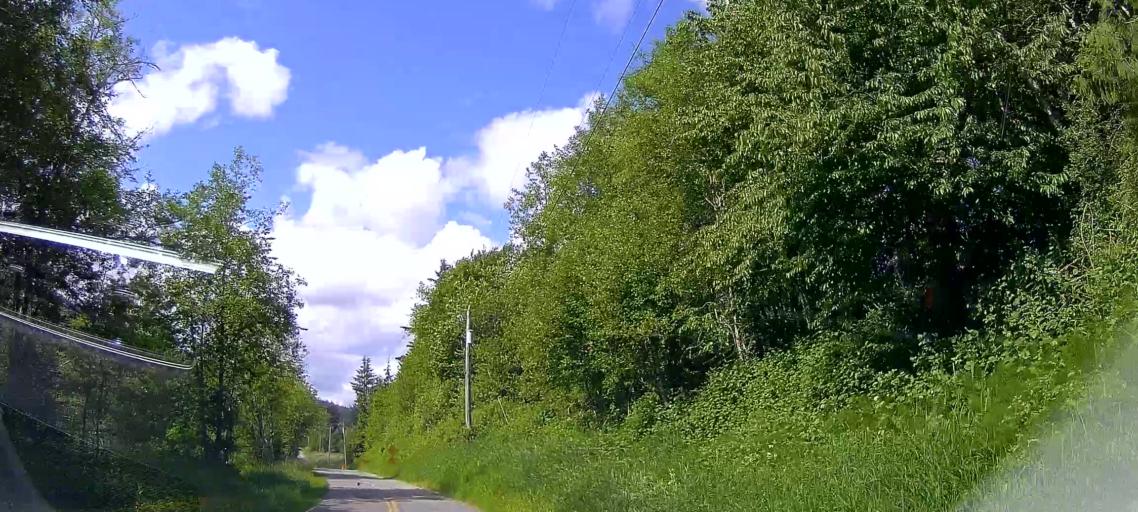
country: US
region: Washington
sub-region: Whatcom County
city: Sudden Valley
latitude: 48.6698
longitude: -122.1948
